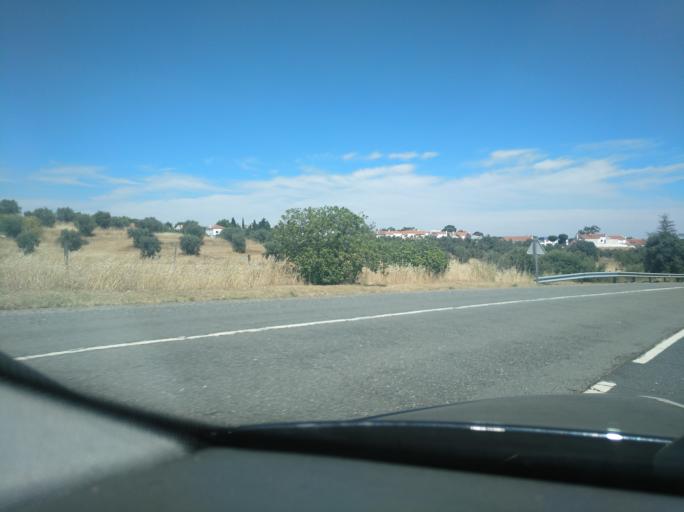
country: PT
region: Beja
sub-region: Castro Verde
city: Castro Verde
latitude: 37.6927
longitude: -8.0875
